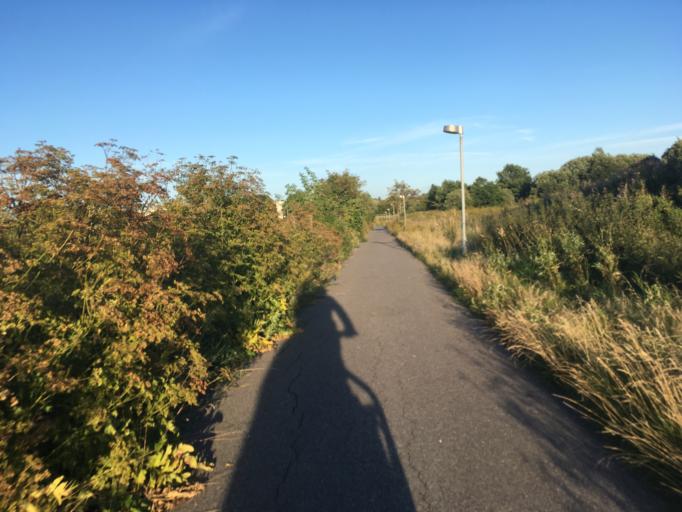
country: DK
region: Capital Region
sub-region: Hillerod Kommune
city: Hillerod
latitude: 55.9256
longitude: 12.2869
